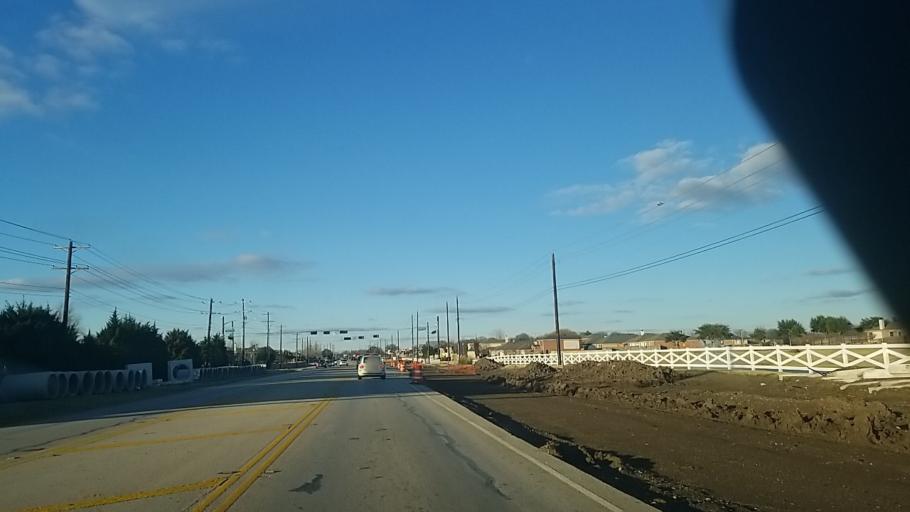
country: US
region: Texas
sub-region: Denton County
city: Corinth
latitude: 33.1527
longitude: -97.1054
